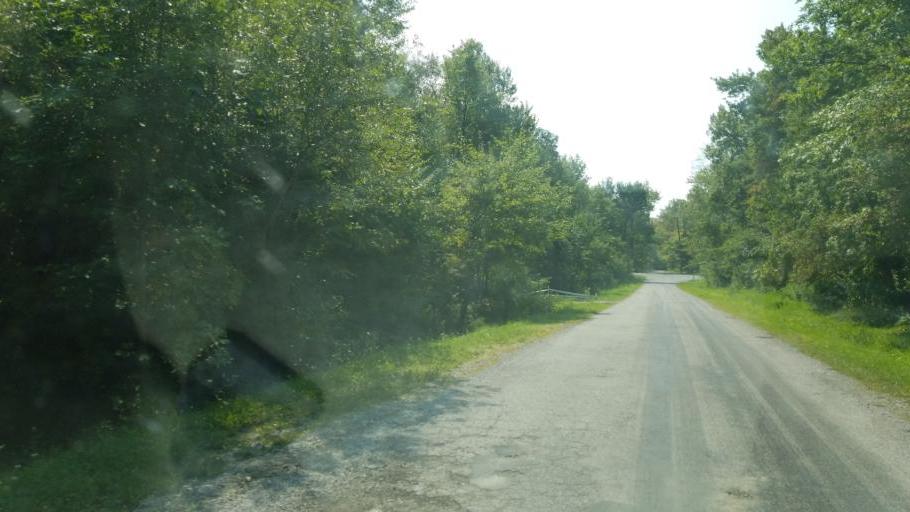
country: US
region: Ohio
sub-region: Lake County
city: Madison
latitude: 41.6349
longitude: -81.0028
